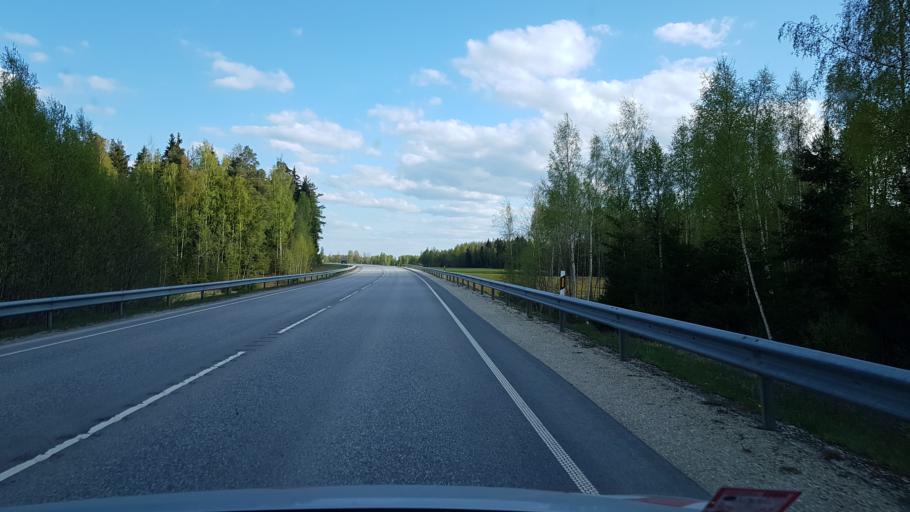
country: EE
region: Vorumaa
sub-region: Voru linn
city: Voru
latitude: 57.9298
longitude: 26.7991
